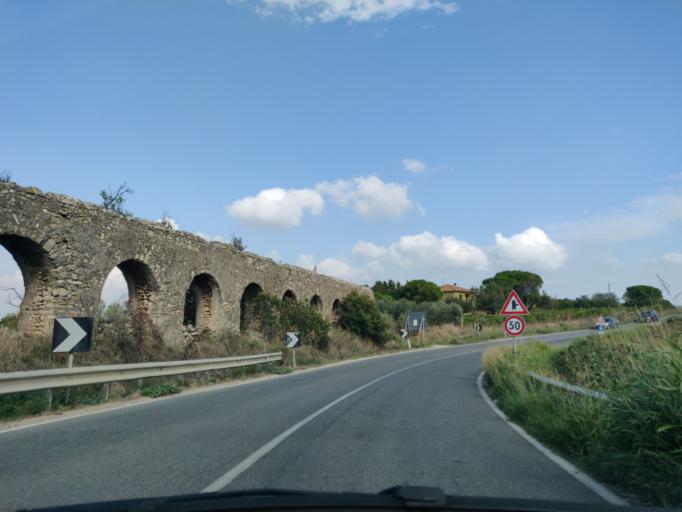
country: IT
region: Latium
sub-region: Provincia di Viterbo
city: Tarquinia
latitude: 42.2379
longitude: 11.7978
